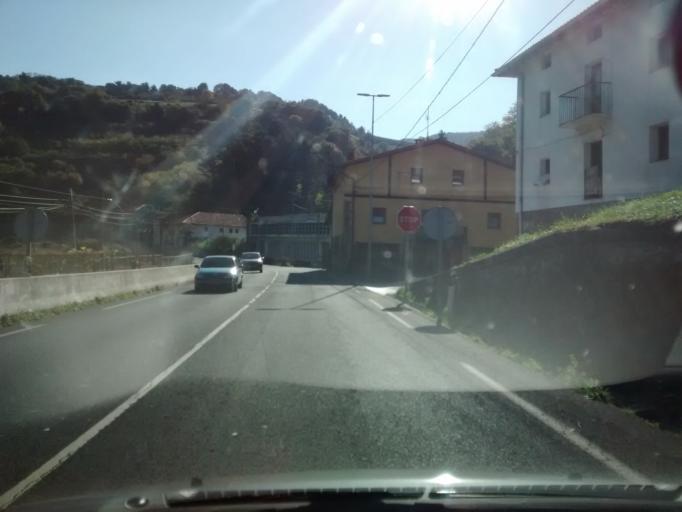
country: ES
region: Basque Country
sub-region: Provincia de Guipuzcoa
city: Deba
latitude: 43.2894
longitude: -2.3624
